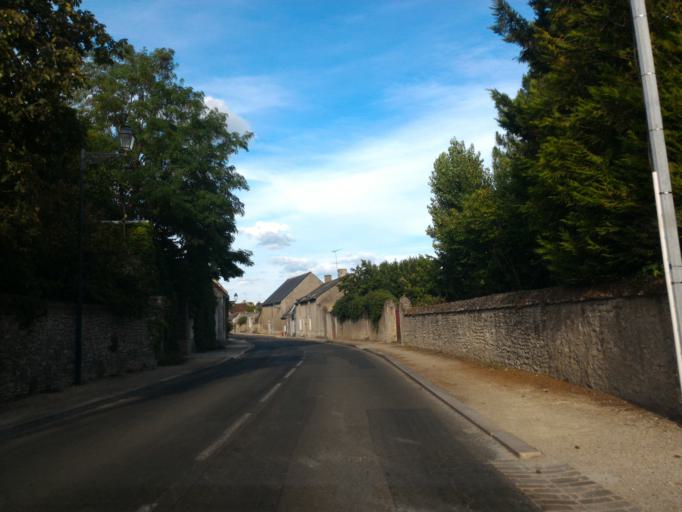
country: FR
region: Centre
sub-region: Departement du Loir-et-Cher
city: Saint-Dye-sur-Loire
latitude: 47.6540
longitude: 1.4828
